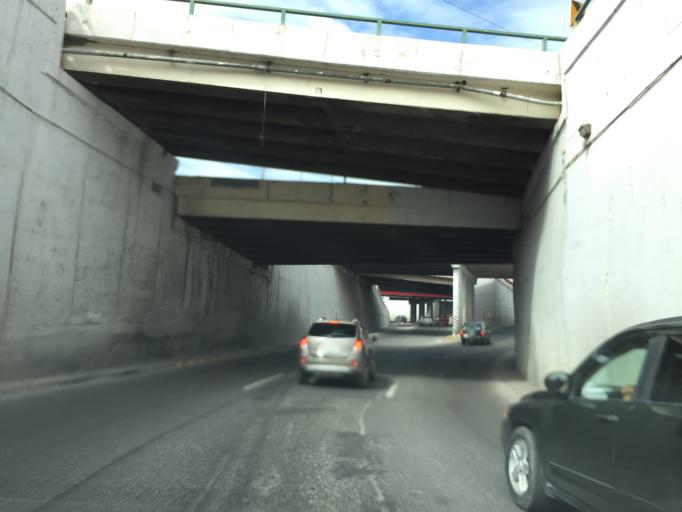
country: MX
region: Nuevo Leon
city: Garza Garcia
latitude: 25.6726
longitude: -100.3519
